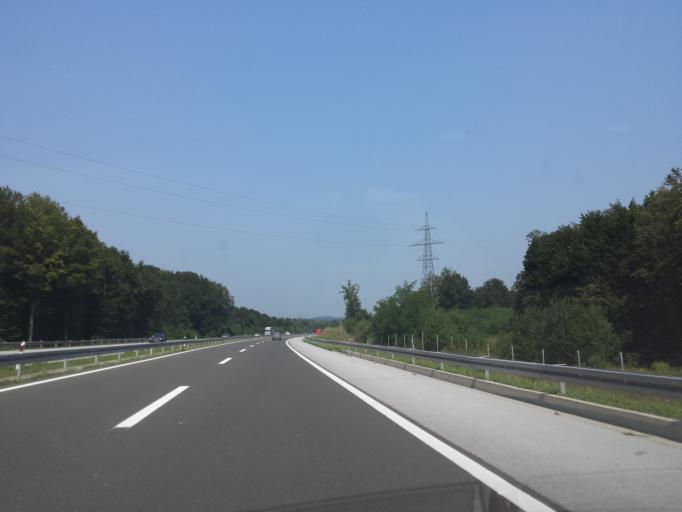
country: HR
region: Karlovacka
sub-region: Grad Ogulin
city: Ogulin
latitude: 45.3633
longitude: 15.2730
